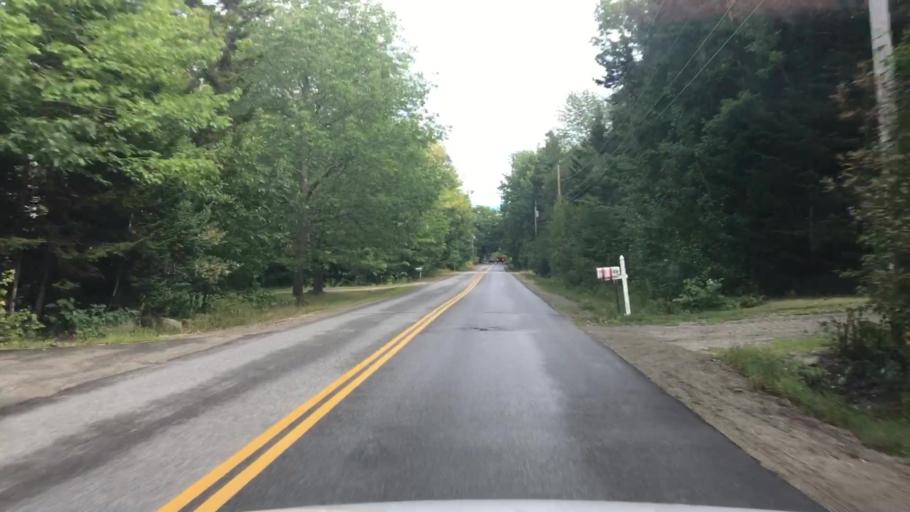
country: US
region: Maine
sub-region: Hancock County
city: Trenton
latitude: 44.4379
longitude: -68.4011
